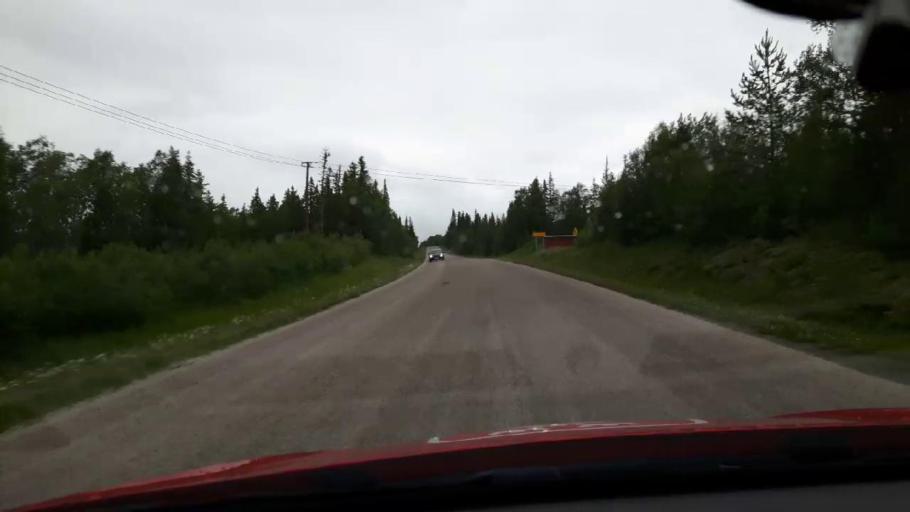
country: NO
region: Nord-Trondelag
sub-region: Meraker
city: Meraker
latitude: 63.2844
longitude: 12.3496
